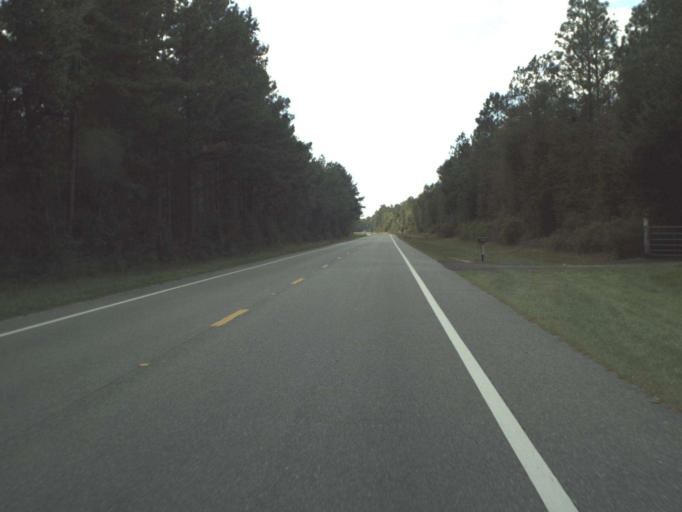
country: US
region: Florida
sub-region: Holmes County
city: Bonifay
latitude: 30.6752
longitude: -85.6398
